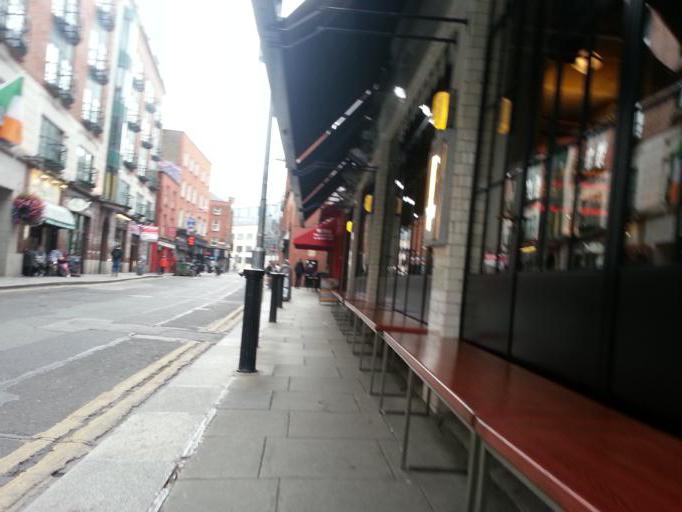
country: IE
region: Leinster
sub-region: Dublin City
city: Dublin
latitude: 53.3413
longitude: -6.2642
